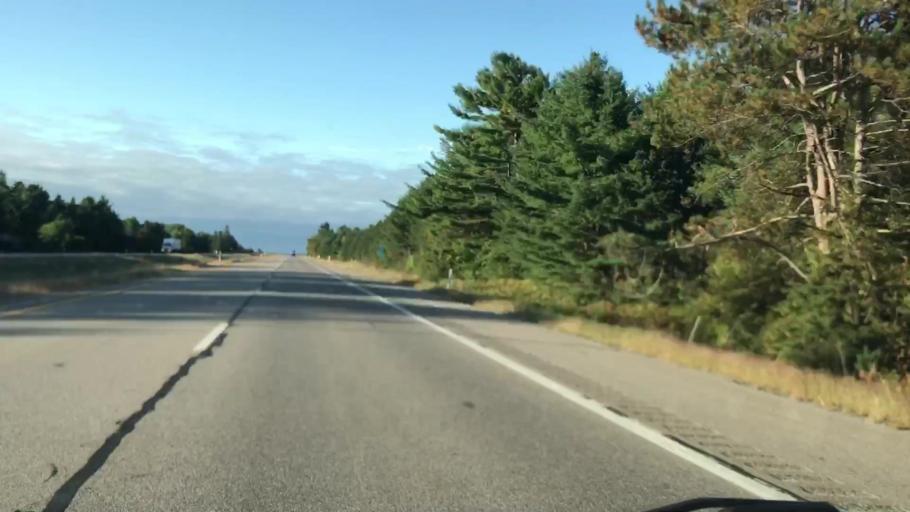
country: US
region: Michigan
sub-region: Chippewa County
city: Sault Ste. Marie
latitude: 46.4318
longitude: -84.3905
